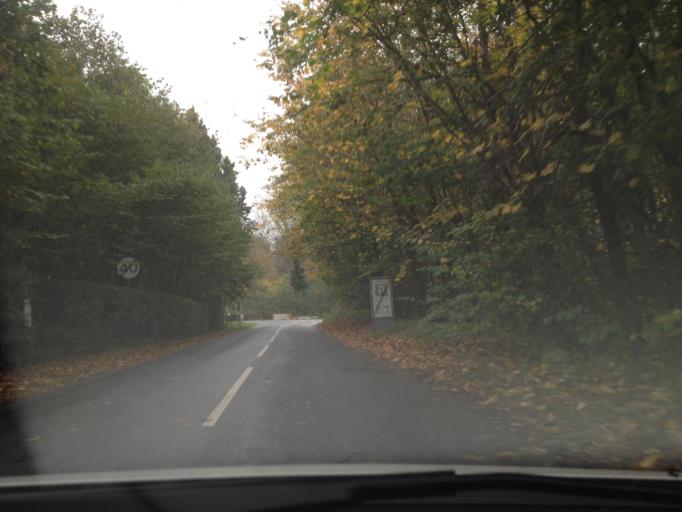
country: DK
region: Capital Region
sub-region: Hillerod Kommune
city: Nodebo
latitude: 55.9644
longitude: 12.3712
